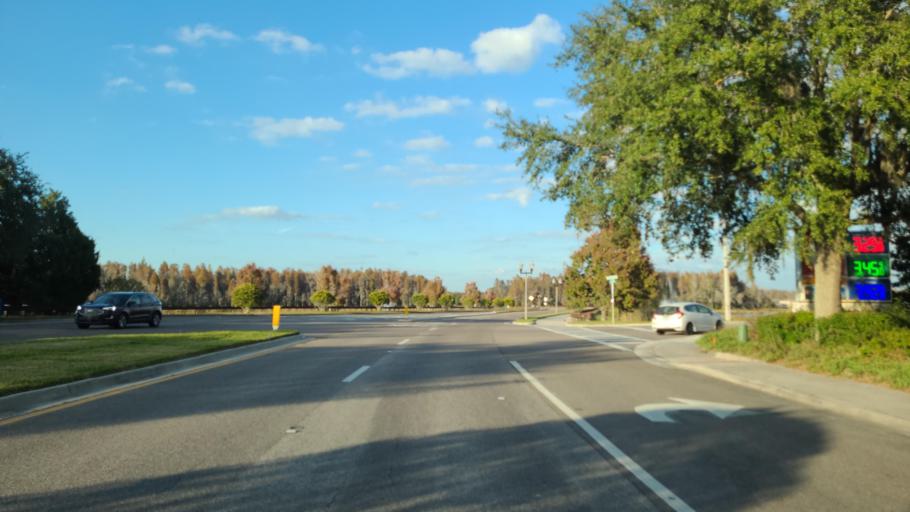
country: US
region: Florida
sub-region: Hillsborough County
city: Cheval
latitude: 28.1954
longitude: -82.5250
